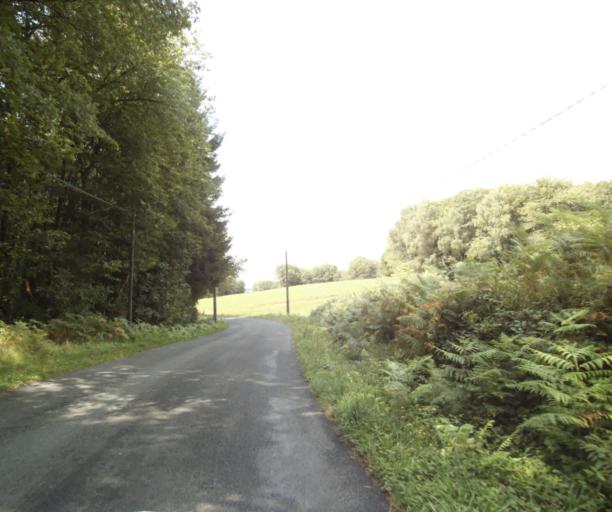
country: FR
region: Limousin
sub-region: Departement de la Correze
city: Sainte-Fortunade
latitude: 45.1765
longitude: 1.7928
